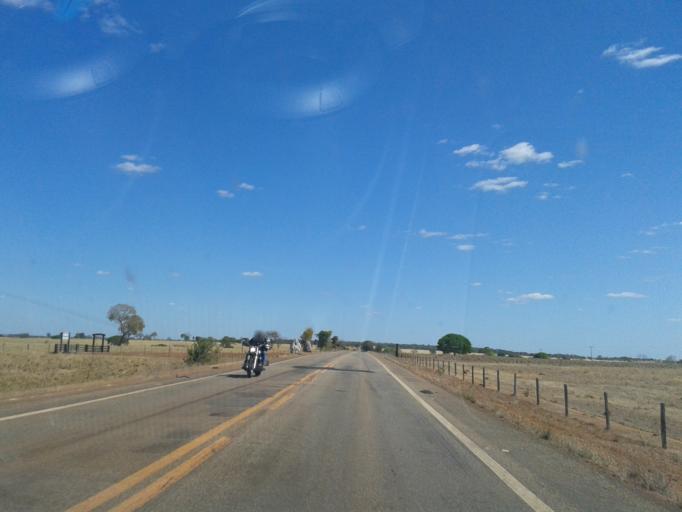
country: BR
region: Goias
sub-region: Sao Miguel Do Araguaia
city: Sao Miguel do Araguaia
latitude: -13.4418
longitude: -50.2895
